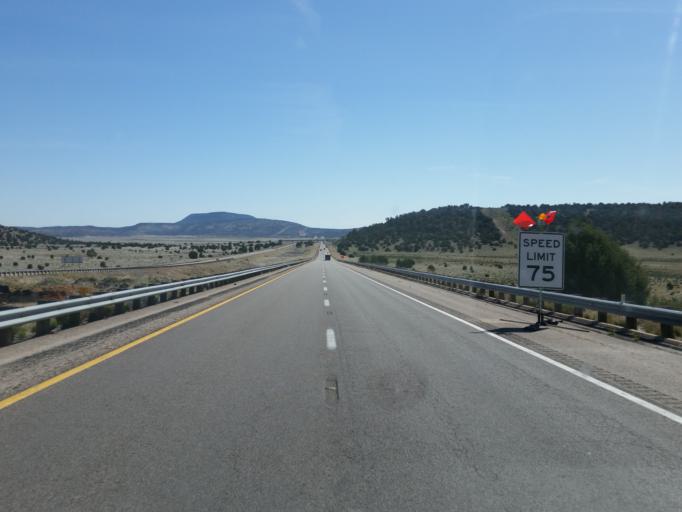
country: US
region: Arizona
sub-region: Mohave County
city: Peach Springs
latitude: 35.2434
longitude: -113.1942
